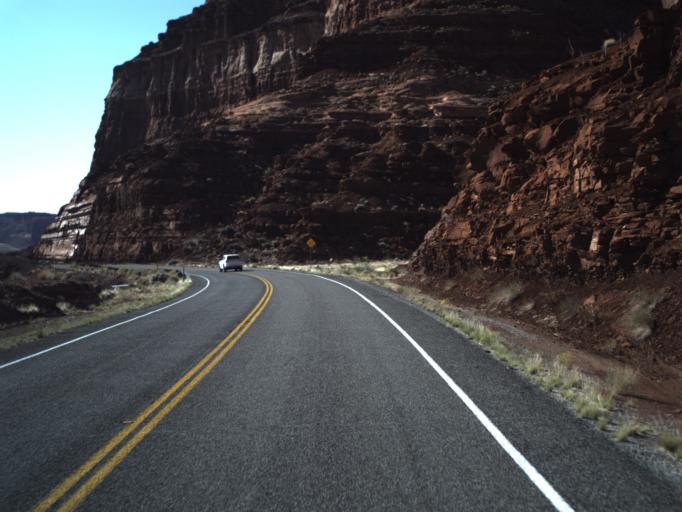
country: US
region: Utah
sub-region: San Juan County
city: Blanding
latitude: 37.9018
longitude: -110.3999
